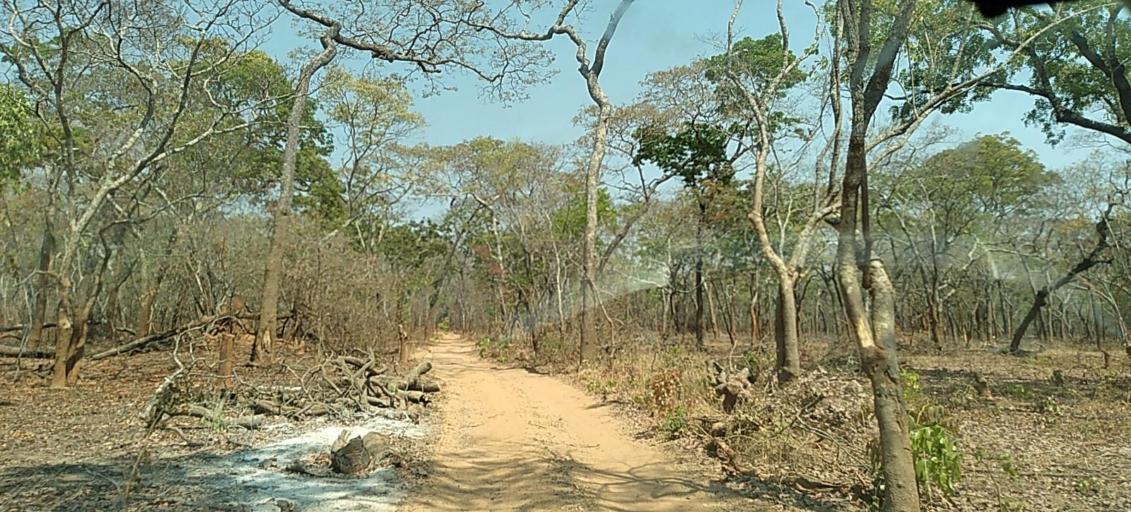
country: ZM
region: North-Western
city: Kasempa
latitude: -13.3928
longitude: 25.6115
